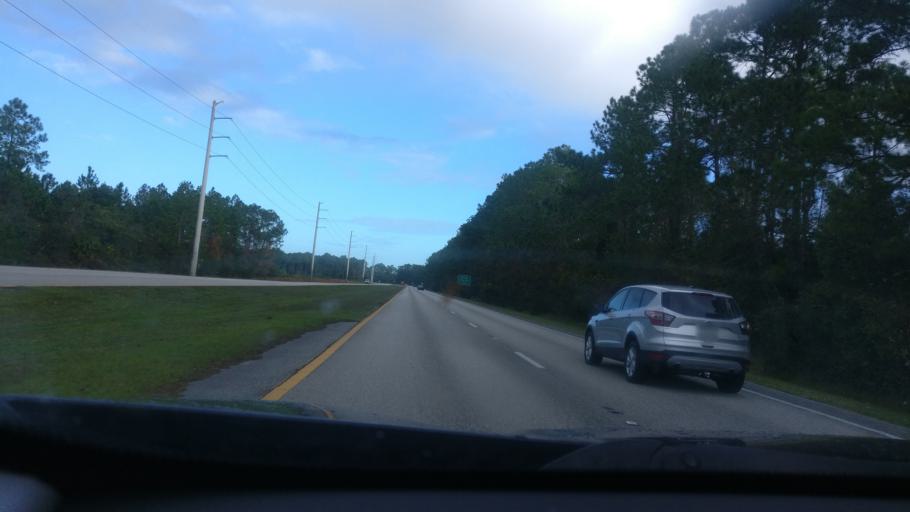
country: US
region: Florida
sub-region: Flagler County
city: Palm Coast
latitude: 29.5426
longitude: -81.2645
